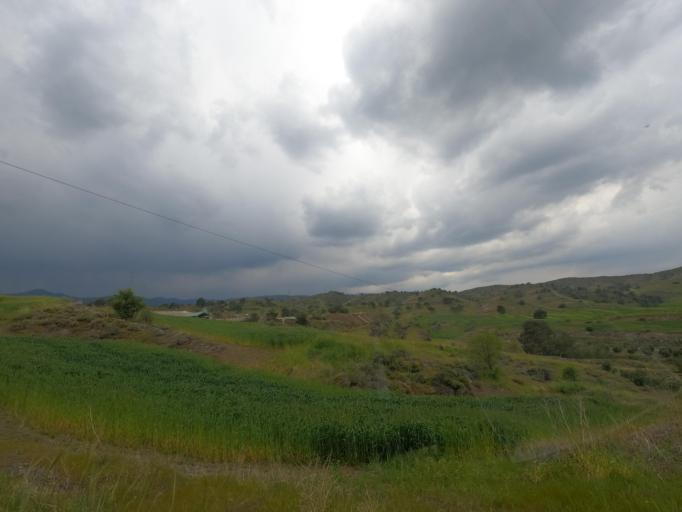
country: CY
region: Lefkosia
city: Lefka
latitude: 35.0809
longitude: 32.9471
